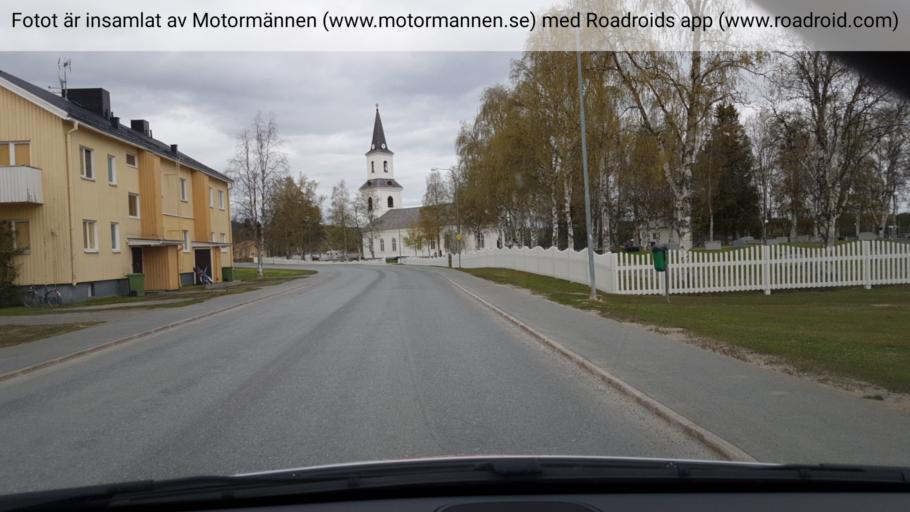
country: SE
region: Vaesterbotten
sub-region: Sorsele Kommun
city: Sorsele
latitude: 65.5408
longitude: 17.5189
